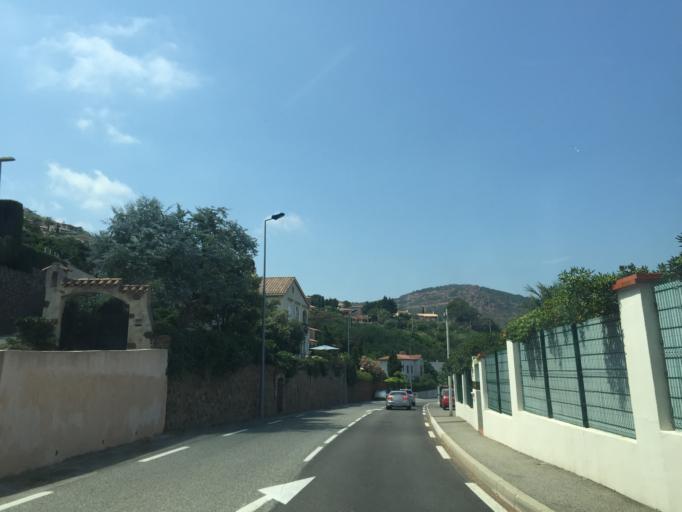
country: FR
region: Provence-Alpes-Cote d'Azur
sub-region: Departement des Alpes-Maritimes
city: Theoule-sur-Mer
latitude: 43.4346
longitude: 6.8938
